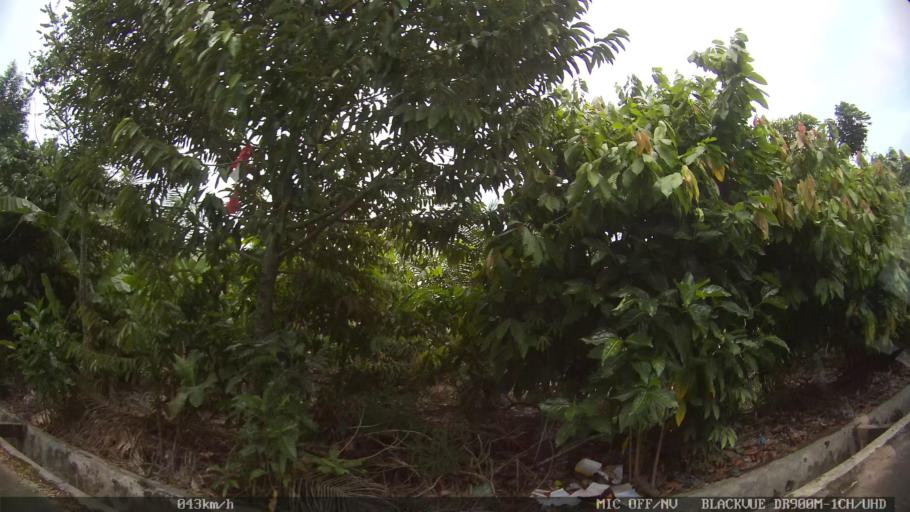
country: ID
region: North Sumatra
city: Sunggal
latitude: 3.6035
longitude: 98.5541
